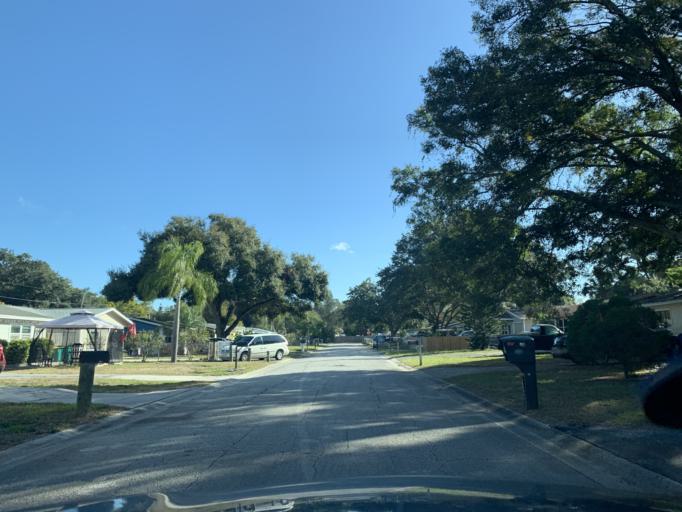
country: US
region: Florida
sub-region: Pinellas County
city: Kenneth City
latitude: 27.8187
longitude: -82.7403
